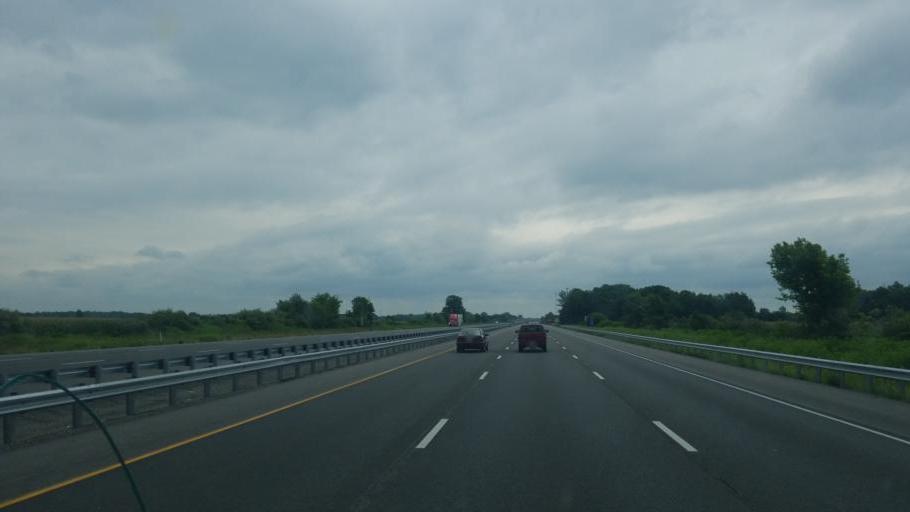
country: US
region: Indiana
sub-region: Madison County
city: Ingalls
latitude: 39.9913
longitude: -85.8103
